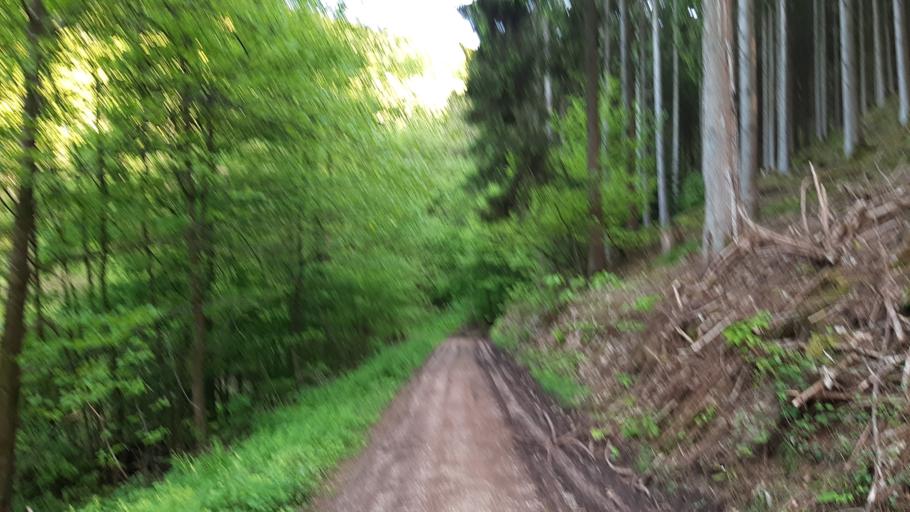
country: DE
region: Rheinland-Pfalz
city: Trierweiler
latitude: 49.7410
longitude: 6.5905
